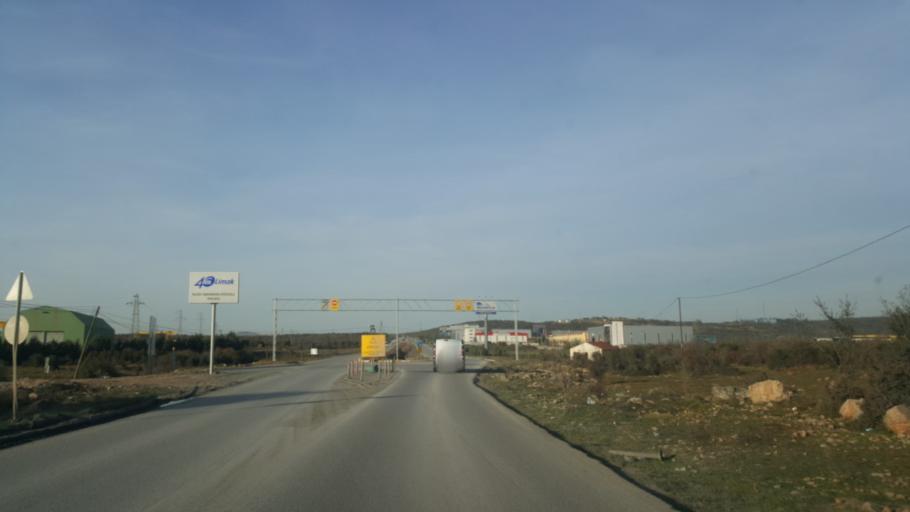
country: TR
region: Kocaeli
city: Tavsanli
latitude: 40.8542
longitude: 29.5554
